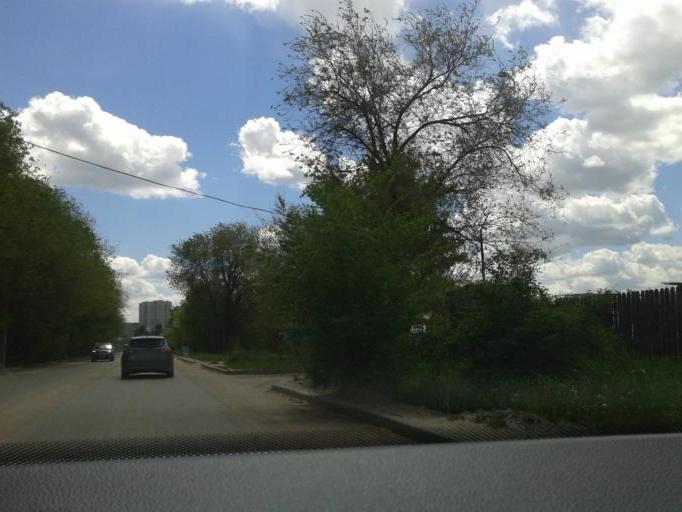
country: RU
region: Volgograd
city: Gorodishche
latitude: 48.7664
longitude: 44.4975
